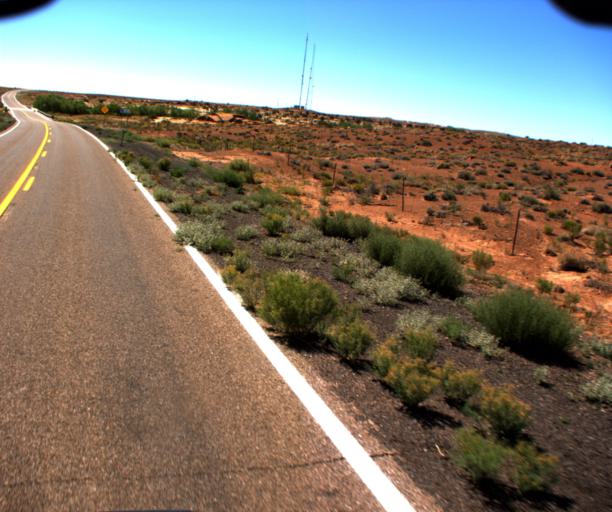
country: US
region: Arizona
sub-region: Navajo County
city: Winslow
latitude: 34.9775
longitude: -110.6558
